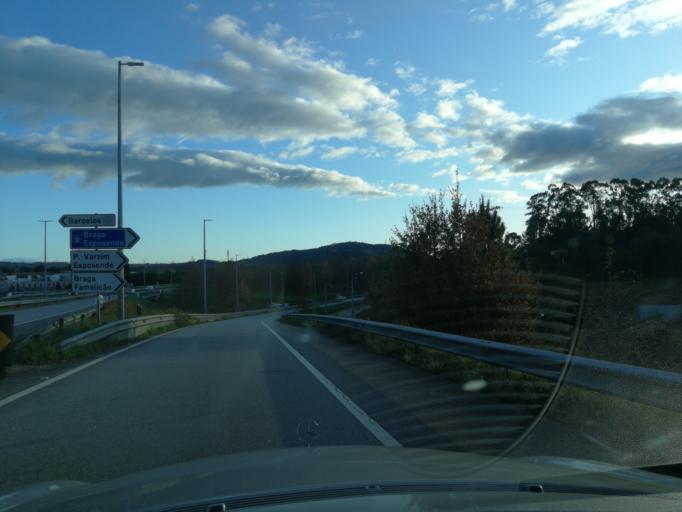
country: PT
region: Braga
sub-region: Barcelos
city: Vila Frescainha
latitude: 41.5363
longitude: -8.6383
